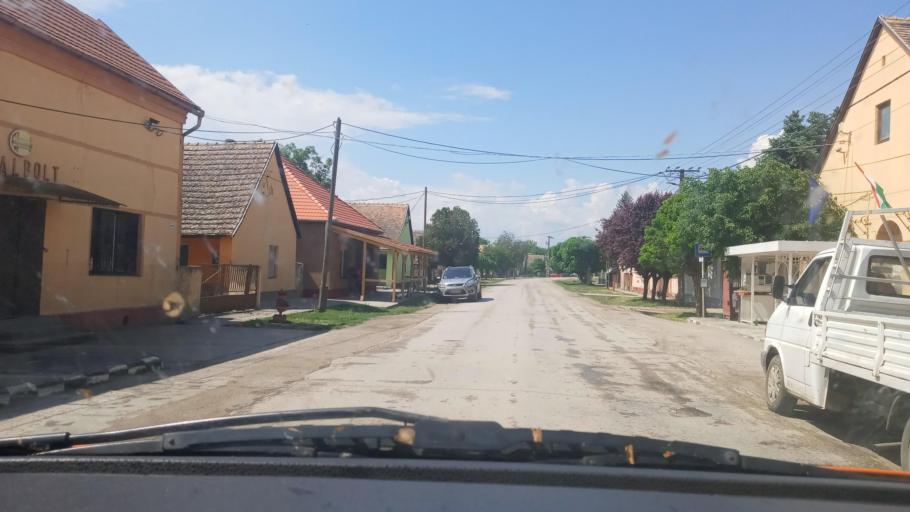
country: HU
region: Baranya
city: Beremend
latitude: 45.7891
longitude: 18.3520
